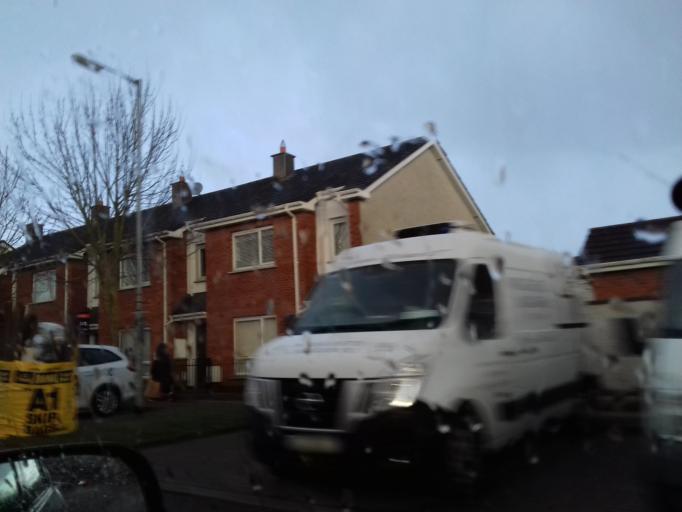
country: IE
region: Leinster
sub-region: Fingal County
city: Blanchardstown
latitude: 53.4020
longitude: -6.3911
